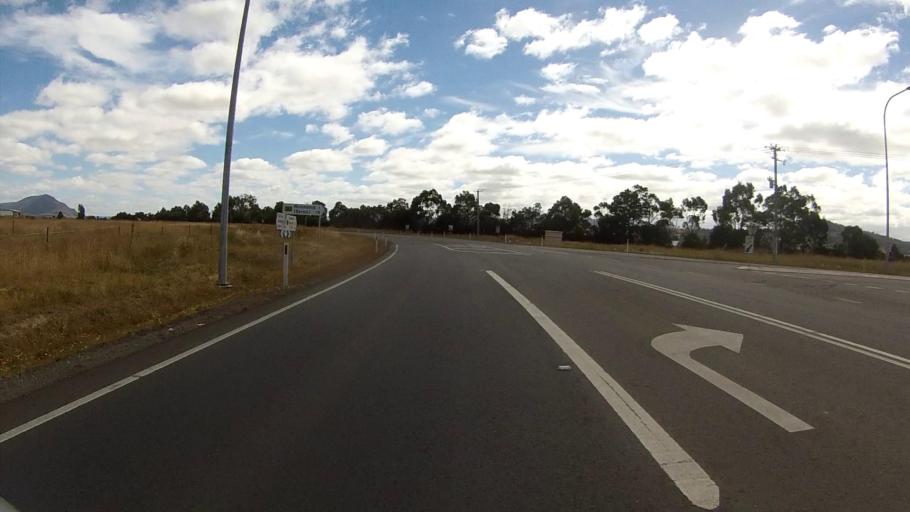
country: AU
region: Tasmania
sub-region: Clarence
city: Cambridge
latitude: -42.7292
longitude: 147.4353
